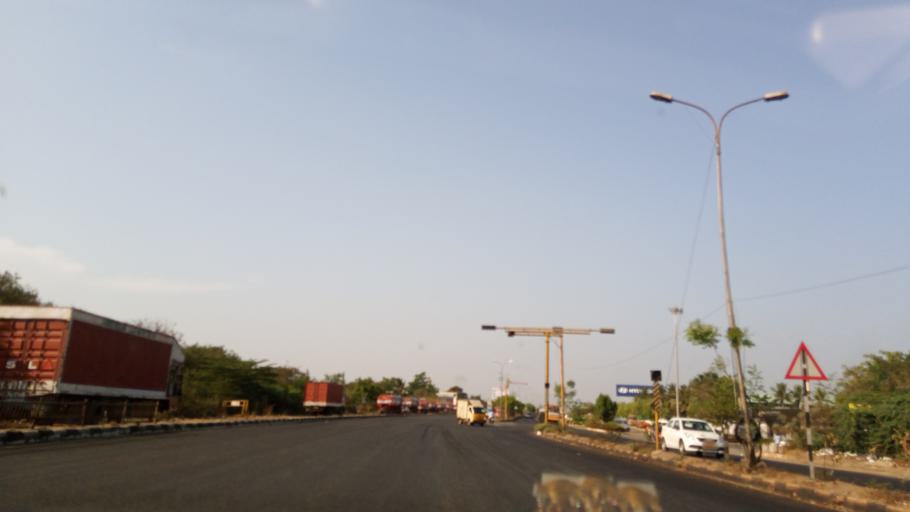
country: IN
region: Tamil Nadu
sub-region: Kancheepuram
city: Sriperumbudur
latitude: 12.9985
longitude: 79.9901
